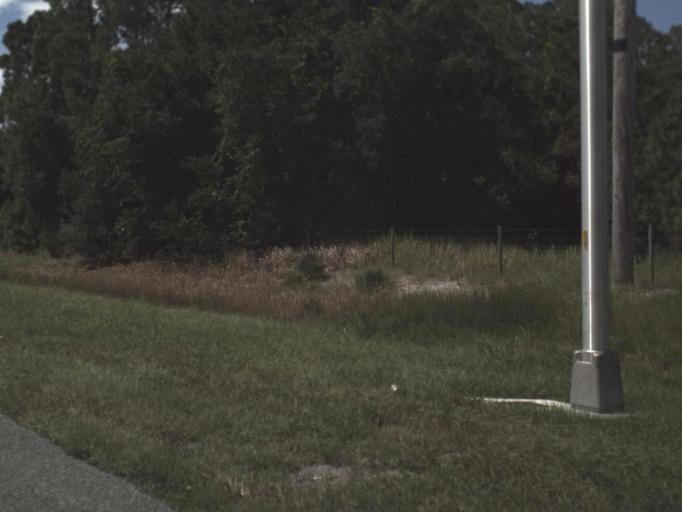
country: US
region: Florida
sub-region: Polk County
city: Babson Park
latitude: 27.8821
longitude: -81.4411
